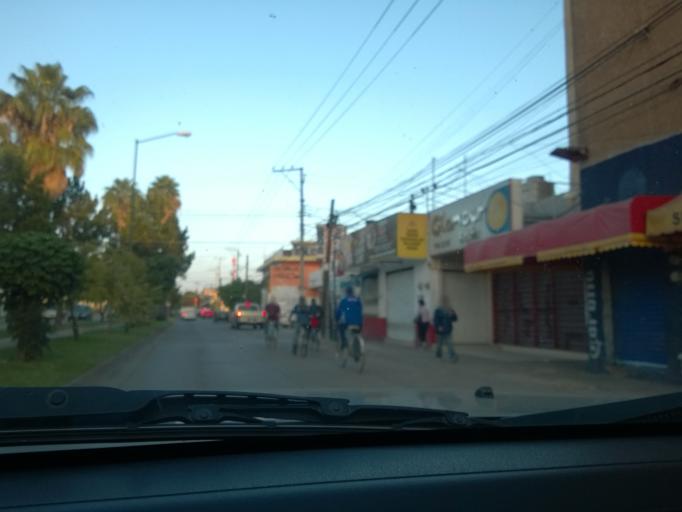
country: MX
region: Guanajuato
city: Leon
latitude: 21.1348
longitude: -101.6574
